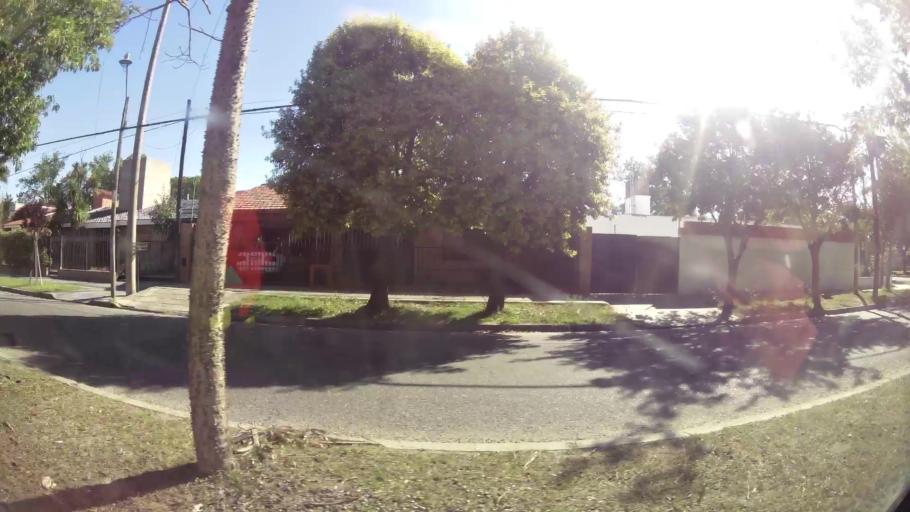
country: AR
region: Cordoba
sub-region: Departamento de Capital
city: Cordoba
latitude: -31.3662
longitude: -64.2004
